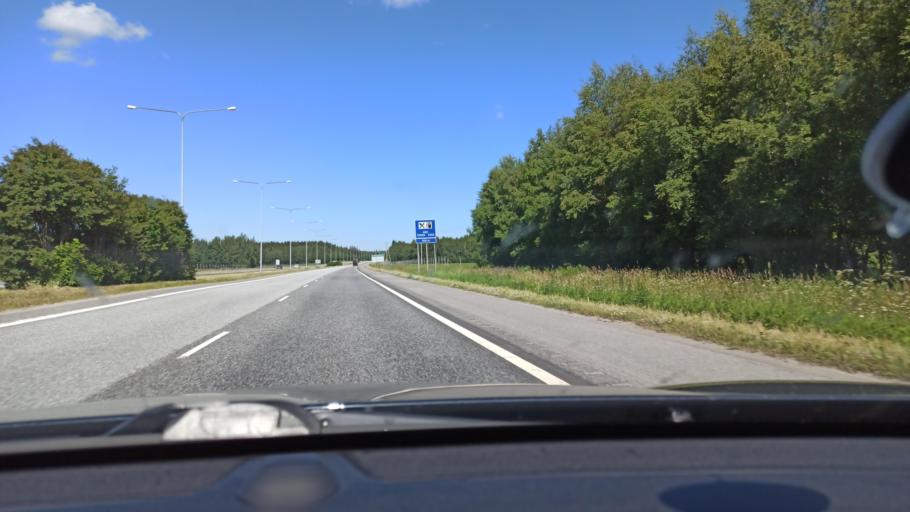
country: FI
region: Ostrobothnia
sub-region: Vaasa
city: Ristinummi
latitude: 63.0436
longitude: 21.7266
